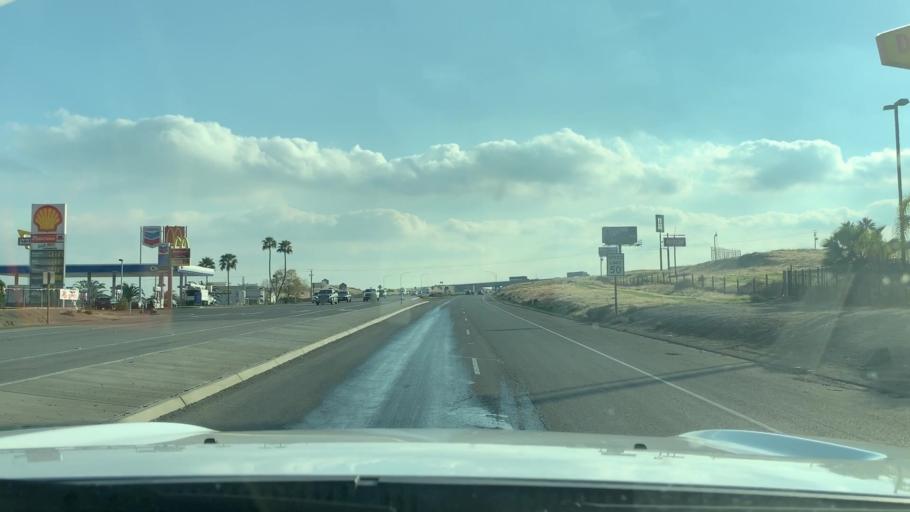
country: US
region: California
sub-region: Kings County
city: Kettleman City
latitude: 35.9878
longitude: -119.9598
